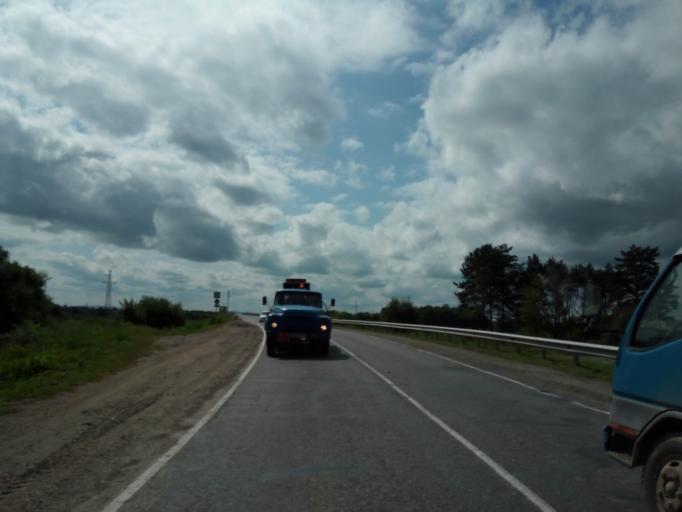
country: RU
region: Primorskiy
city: Dal'nerechensk
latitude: 45.9656
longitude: 133.7829
